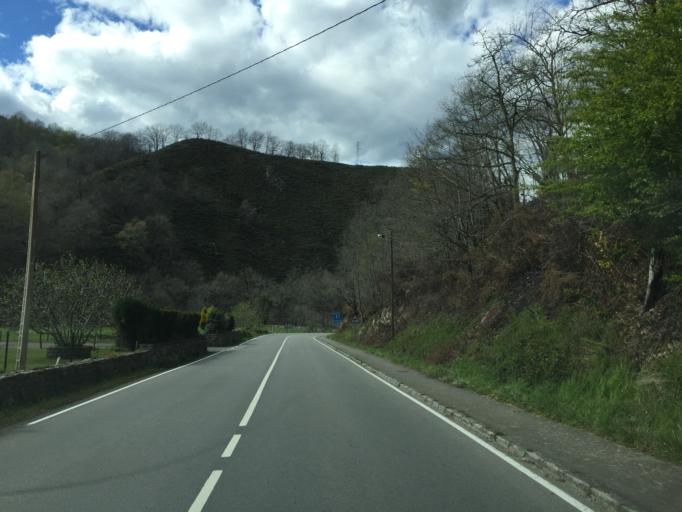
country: ES
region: Asturias
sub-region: Province of Asturias
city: Cangas de Onis
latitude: 43.3280
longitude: -5.0799
